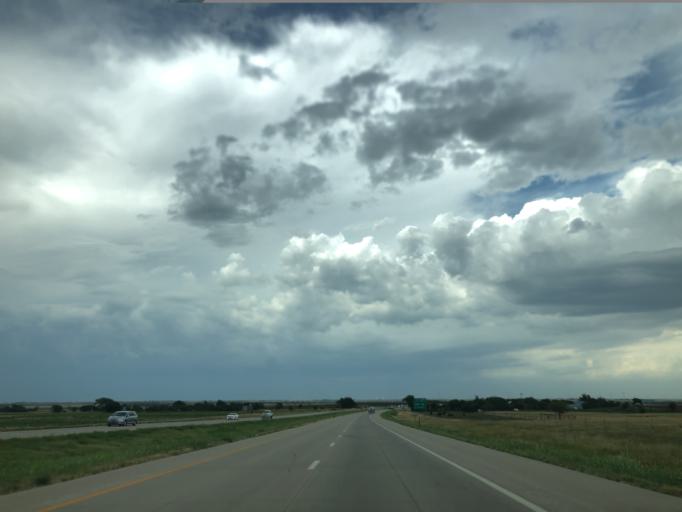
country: US
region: Kansas
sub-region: Ellsworth County
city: Ellsworth
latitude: 38.8485
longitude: -98.4205
